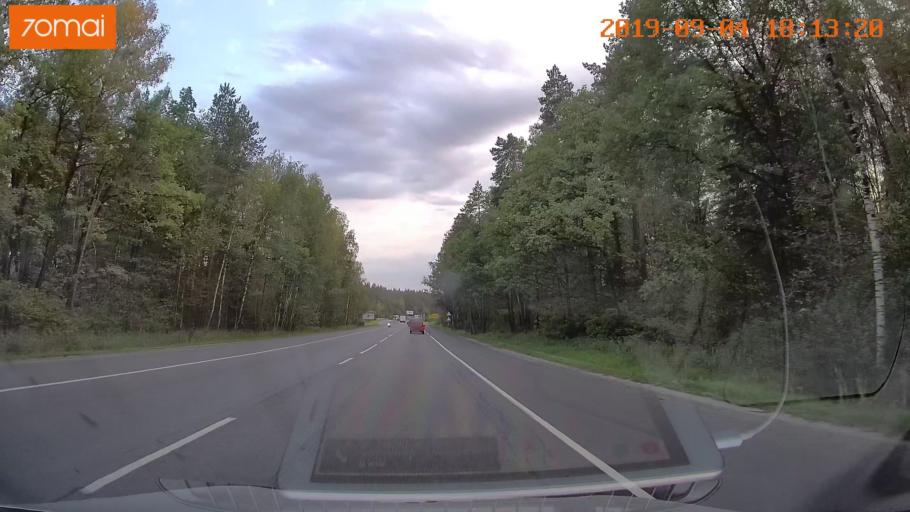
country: RU
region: Moskovskaya
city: Lopatinskiy
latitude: 55.3614
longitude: 38.7347
